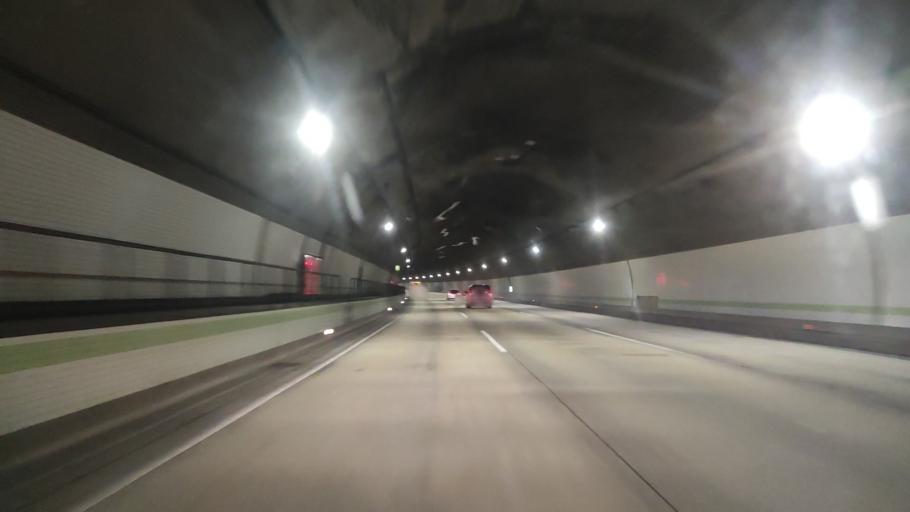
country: JP
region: Hyogo
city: Akashi
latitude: 34.6427
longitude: 135.0475
